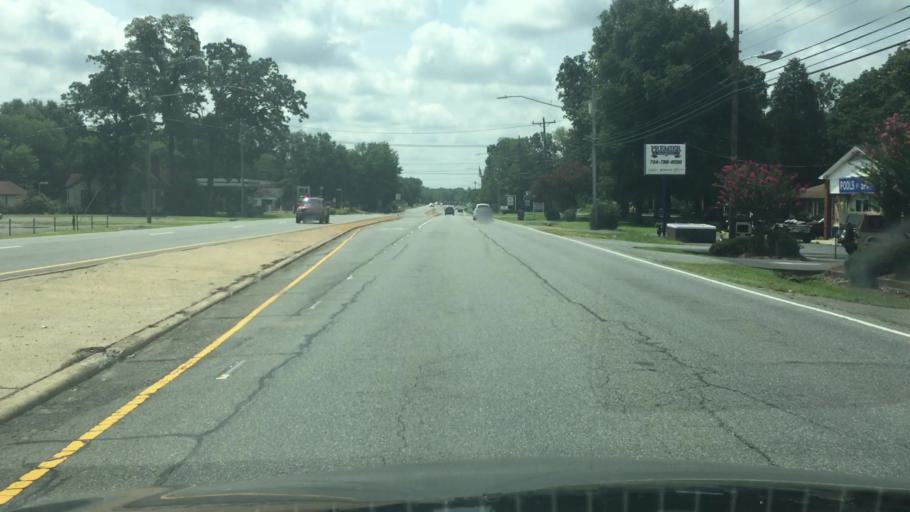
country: US
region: North Carolina
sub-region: Cabarrus County
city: Kannapolis
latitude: 35.4632
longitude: -80.6093
